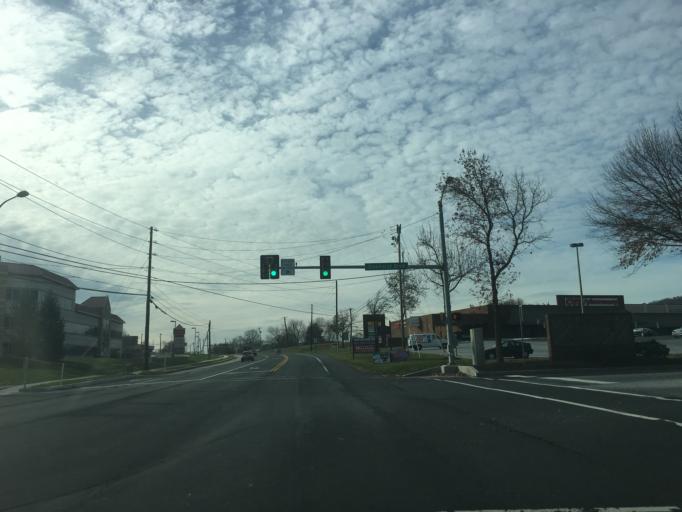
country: US
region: Pennsylvania
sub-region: Dauphin County
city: Lawrence Park
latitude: 40.3320
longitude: -76.8481
